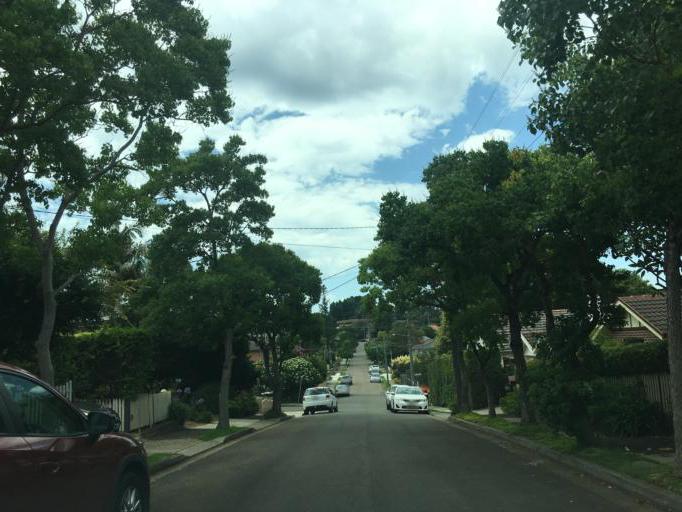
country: AU
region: New South Wales
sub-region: Hunters Hill
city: Gladesville
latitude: -33.8333
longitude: 151.1227
